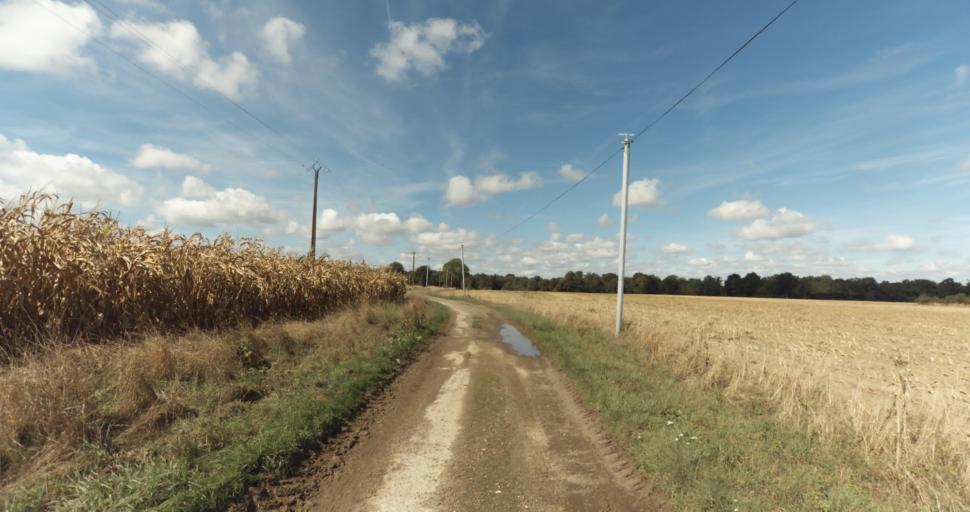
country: FR
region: Lower Normandy
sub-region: Departement du Calvados
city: Orbec
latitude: 48.9628
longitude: 0.4041
